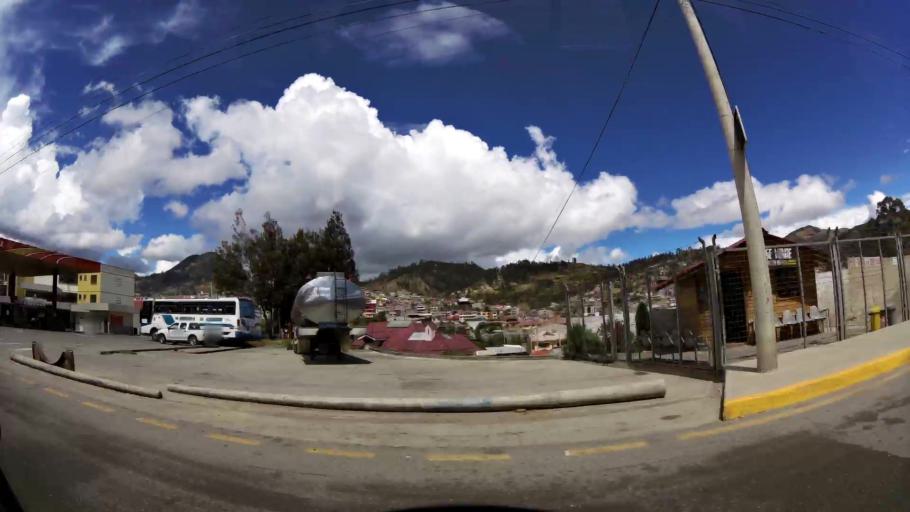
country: EC
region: Canar
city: Azogues
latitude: -2.7480
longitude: -78.8510
